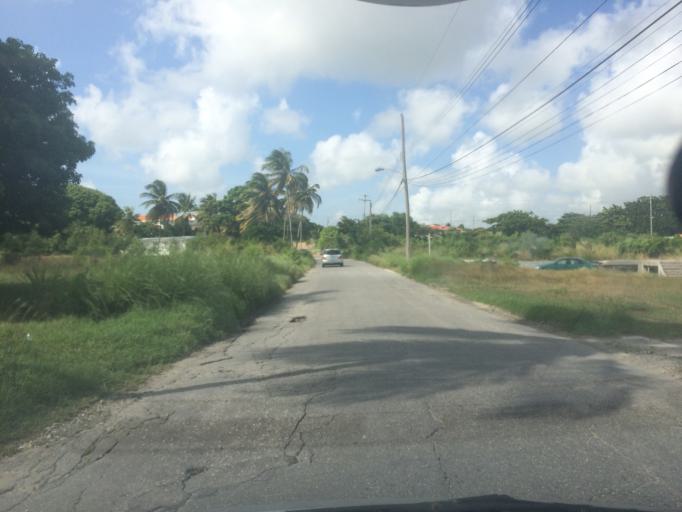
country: BB
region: Christ Church
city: Oistins
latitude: 13.0737
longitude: -59.5107
